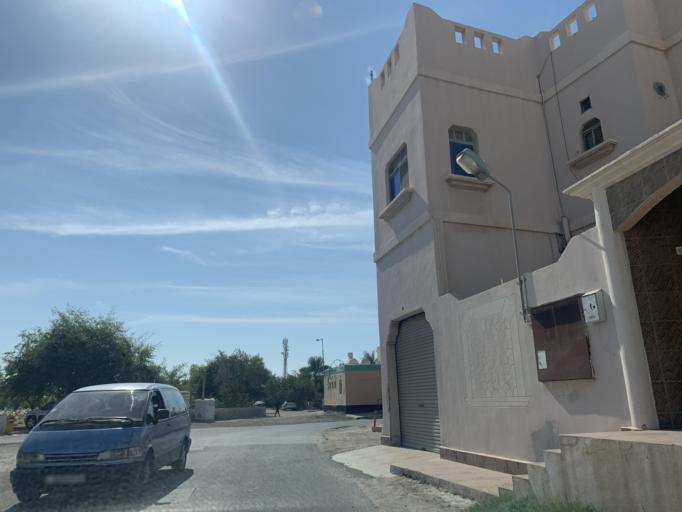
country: BH
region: Central Governorate
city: Madinat Hamad
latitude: 26.1156
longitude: 50.4829
